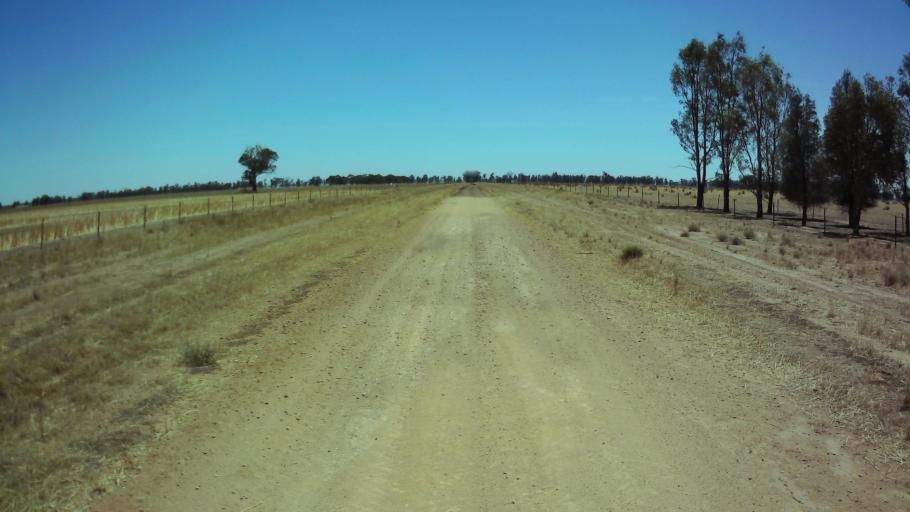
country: AU
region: New South Wales
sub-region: Weddin
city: Grenfell
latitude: -33.9853
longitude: 147.7352
